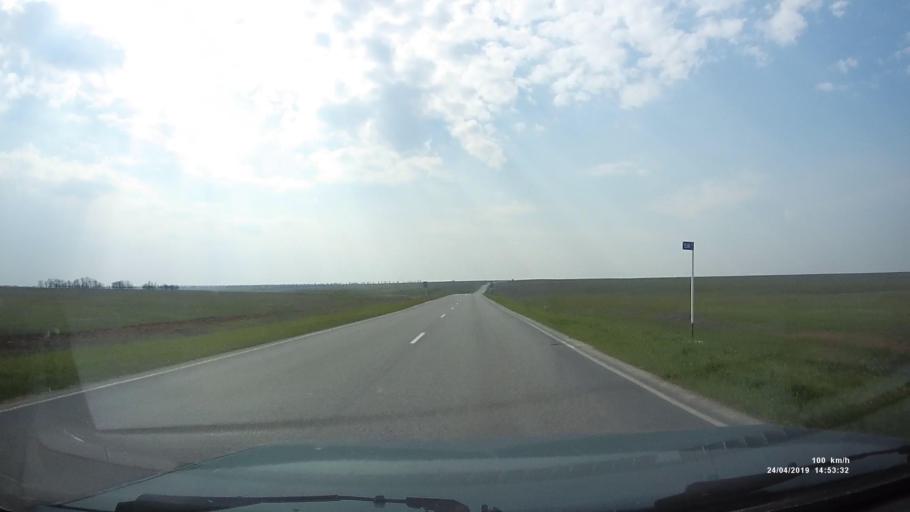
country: RU
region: Rostov
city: Remontnoye
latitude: 46.5314
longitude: 43.6568
